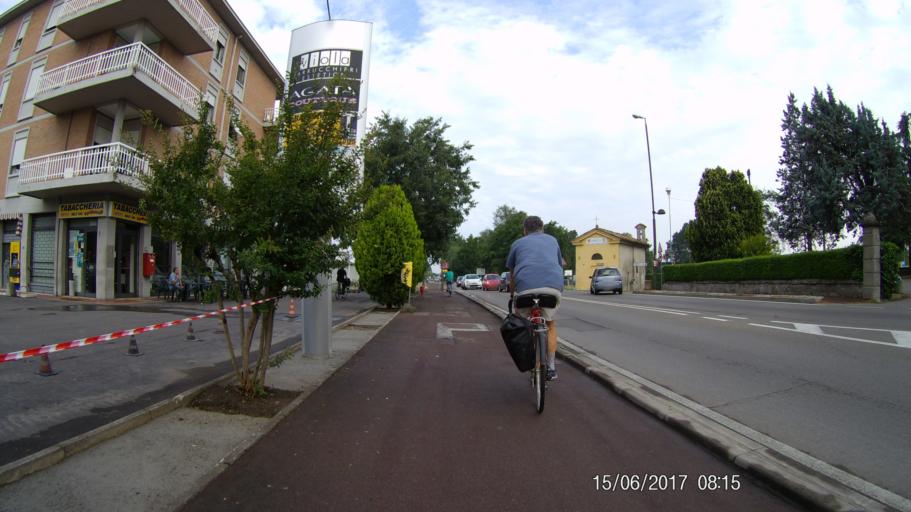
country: IT
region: Emilia-Romagna
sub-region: Provincia di Reggio Emilia
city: Roncocesi
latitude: 44.7139
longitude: 10.5868
